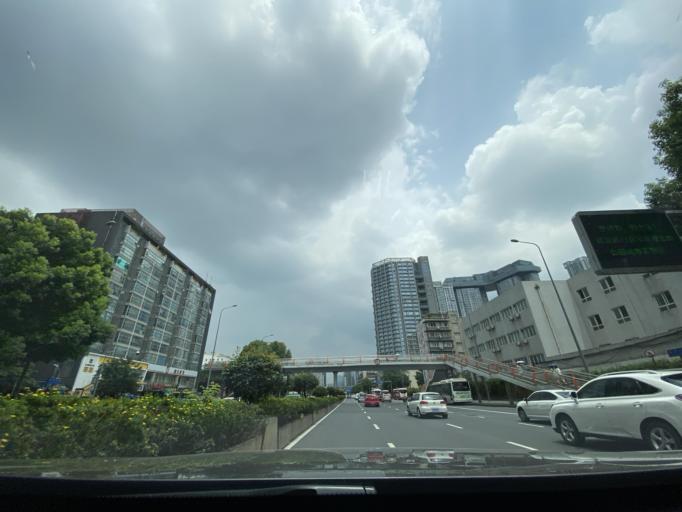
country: CN
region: Sichuan
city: Chengdu
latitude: 30.6172
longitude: 104.0747
